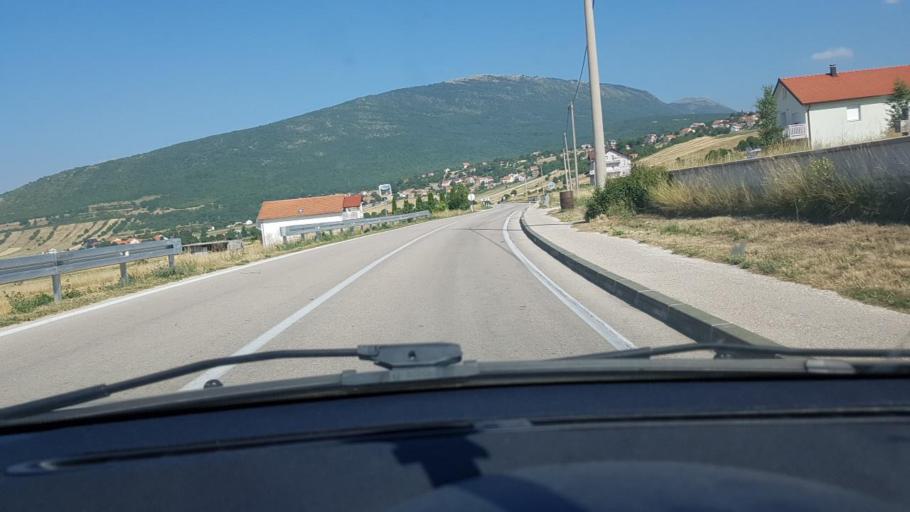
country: BA
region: Federation of Bosnia and Herzegovina
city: Zabrisce
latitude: 43.8672
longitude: 16.9284
